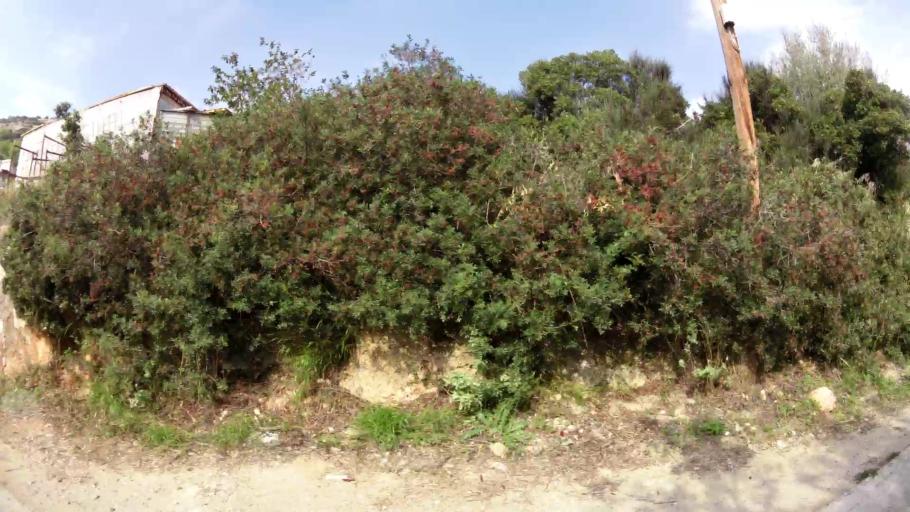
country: GR
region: Attica
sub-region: Nomarchia Athinas
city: Petroupolis
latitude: 38.0544
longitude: 23.6910
